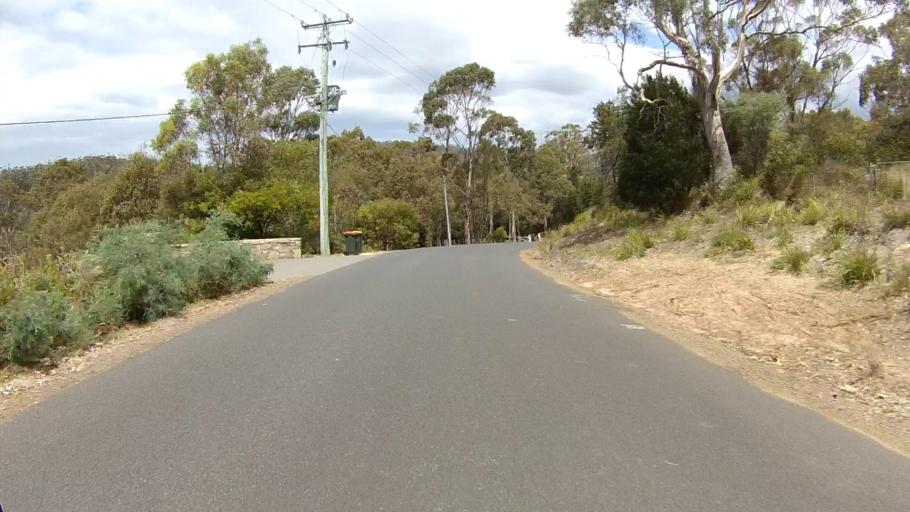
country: AU
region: Tasmania
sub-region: Sorell
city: Sorell
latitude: -42.5889
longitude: 147.9148
